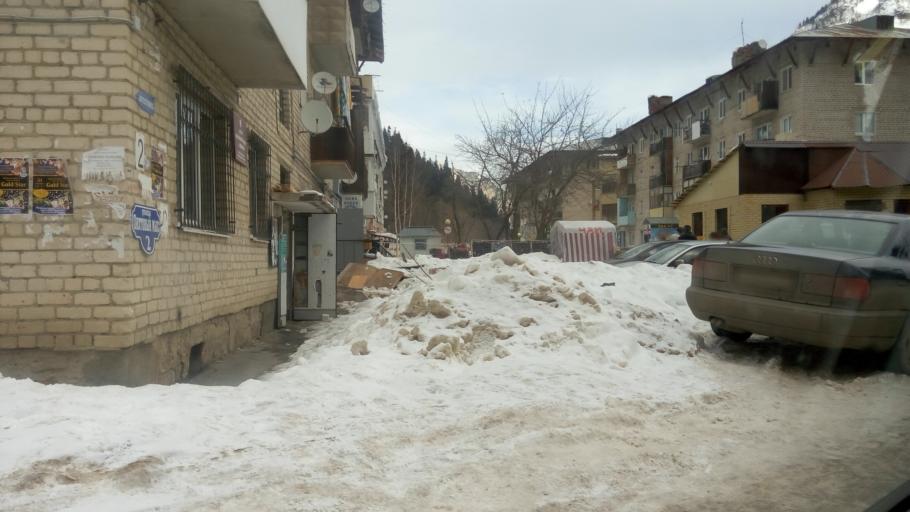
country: RU
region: Karachayevo-Cherkesiya
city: Teberda
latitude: 43.2883
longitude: 41.6196
